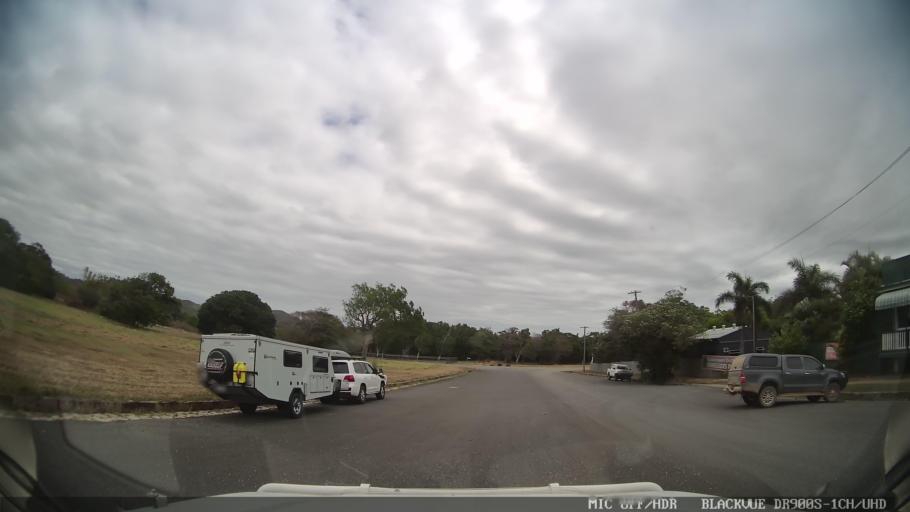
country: AU
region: Queensland
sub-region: Cook
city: Cooktown
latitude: -15.4697
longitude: 145.2486
